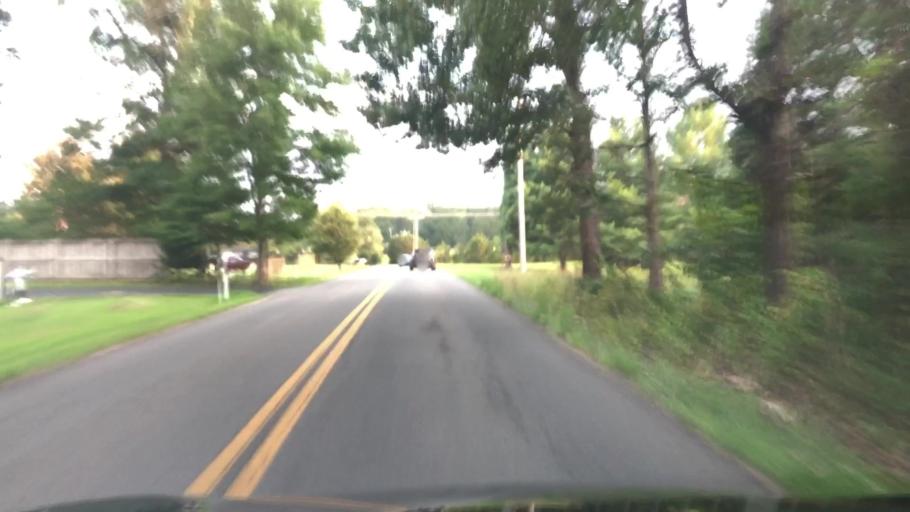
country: US
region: Virginia
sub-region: Fauquier County
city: Bealeton
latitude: 38.5112
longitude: -77.6842
